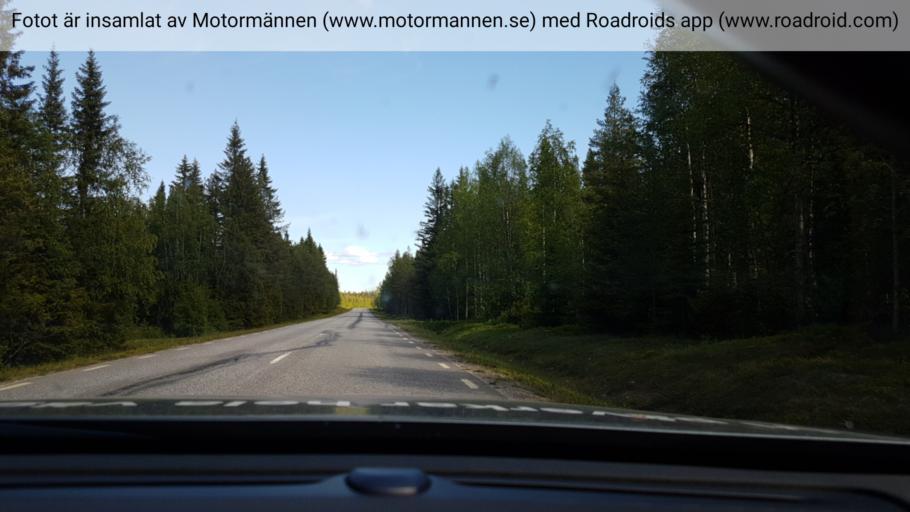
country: SE
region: Vaesterbotten
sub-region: Lycksele Kommun
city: Soderfors
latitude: 64.6232
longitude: 18.1131
